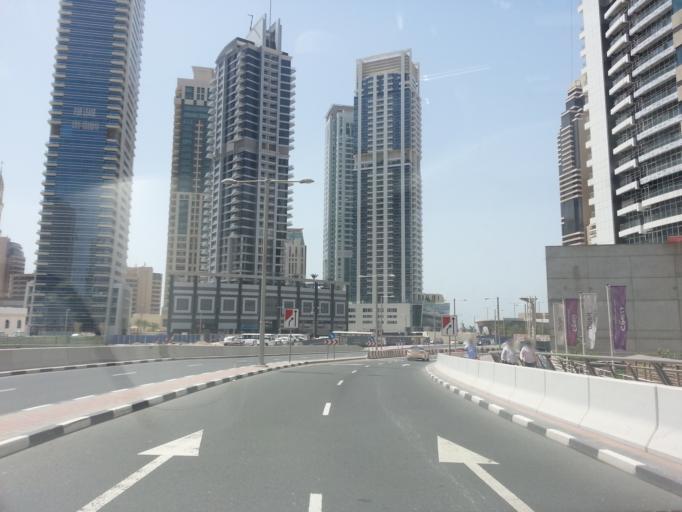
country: AE
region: Dubai
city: Dubai
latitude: 25.0829
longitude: 55.1439
